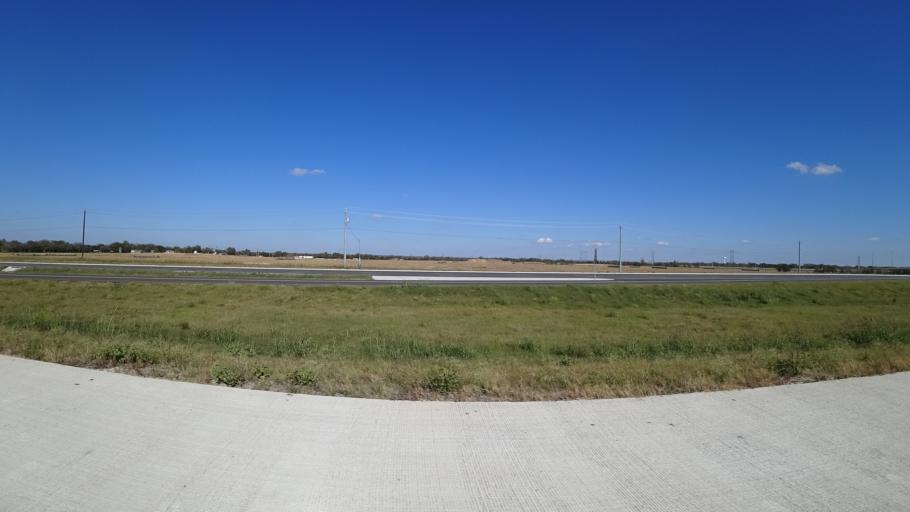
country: US
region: Texas
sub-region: Travis County
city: Hornsby Bend
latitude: 30.1999
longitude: -97.6336
